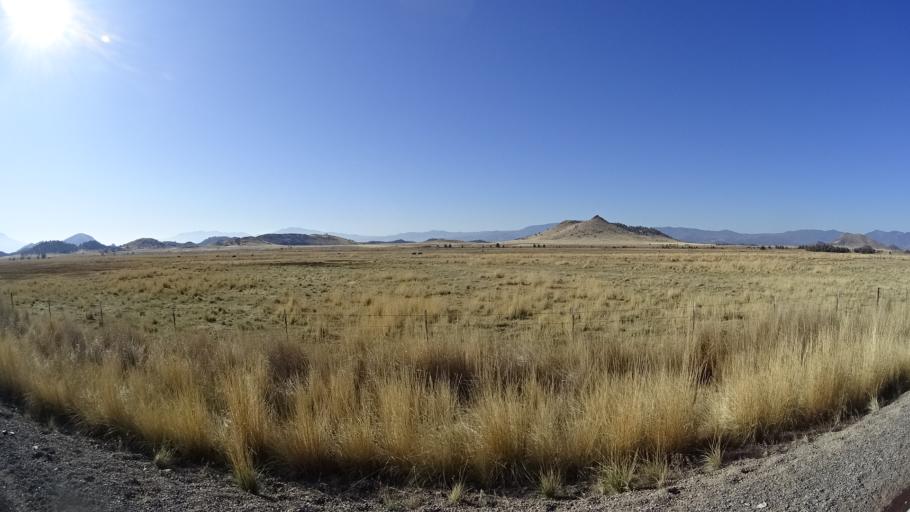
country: US
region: California
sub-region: Siskiyou County
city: Montague
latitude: 41.7137
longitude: -122.4406
